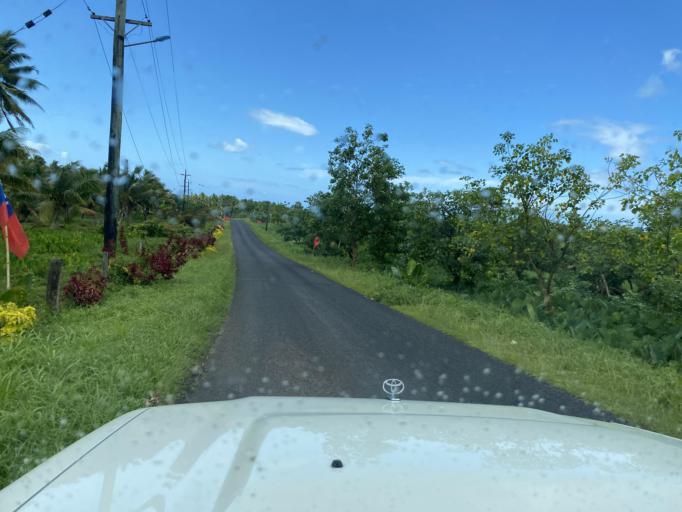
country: WS
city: Matavai
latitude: -13.9916
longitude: -171.5854
